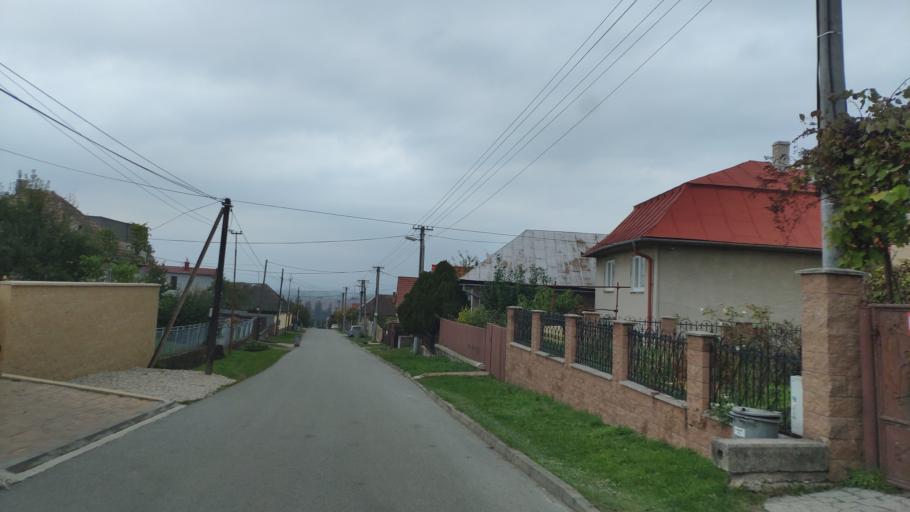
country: SK
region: Kosicky
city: Kosice
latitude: 48.6356
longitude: 21.3886
